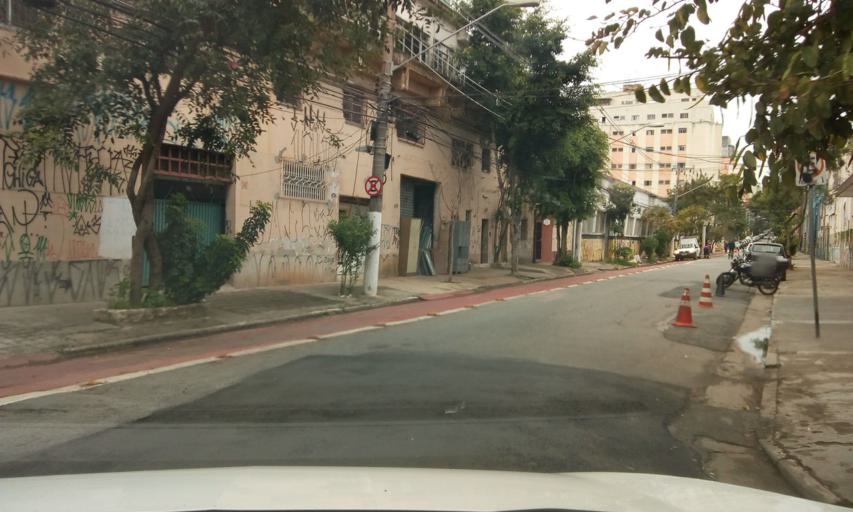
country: BR
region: Sao Paulo
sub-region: Sao Paulo
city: Sao Paulo
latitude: -23.5289
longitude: -46.6507
